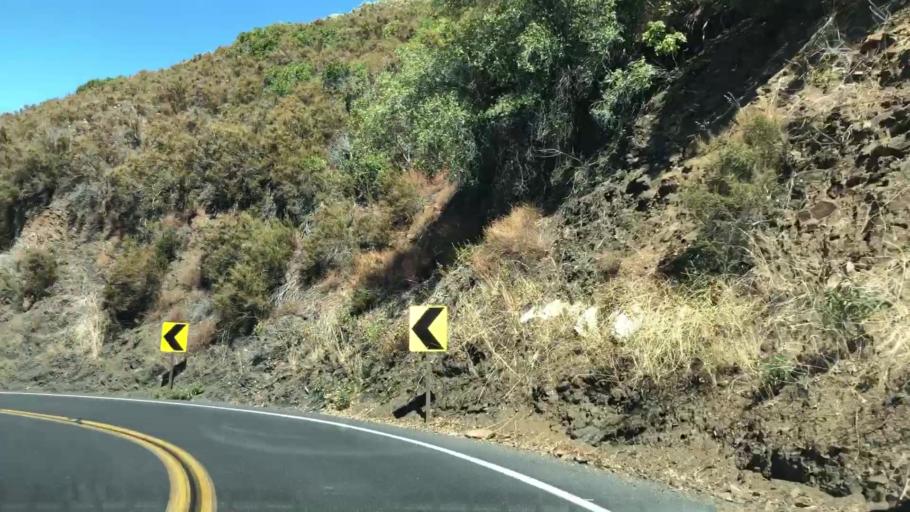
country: US
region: California
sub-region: Tuolumne County
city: Tuolumne City
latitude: 37.8189
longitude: -120.2741
